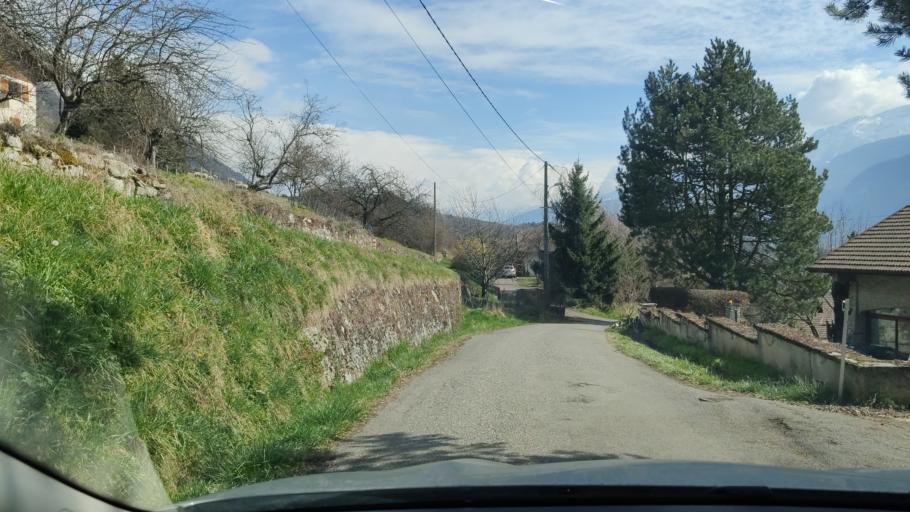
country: FR
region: Rhone-Alpes
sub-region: Departement de la Haute-Savoie
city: Bonneville
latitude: 46.0889
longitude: 6.4028
